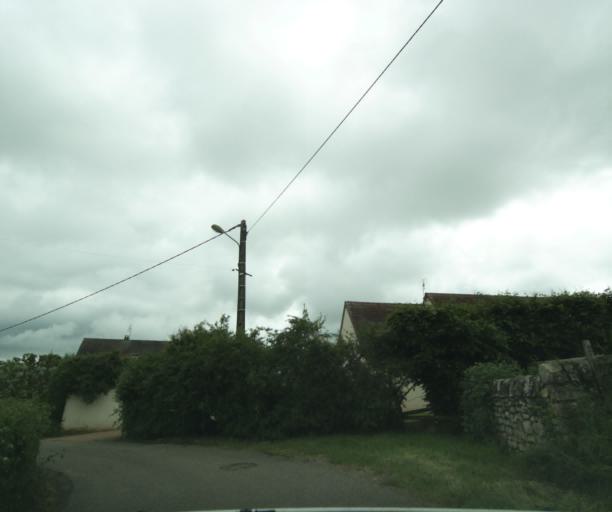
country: FR
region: Bourgogne
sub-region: Departement de Saone-et-Loire
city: Charolles
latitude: 46.4346
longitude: 4.2630
